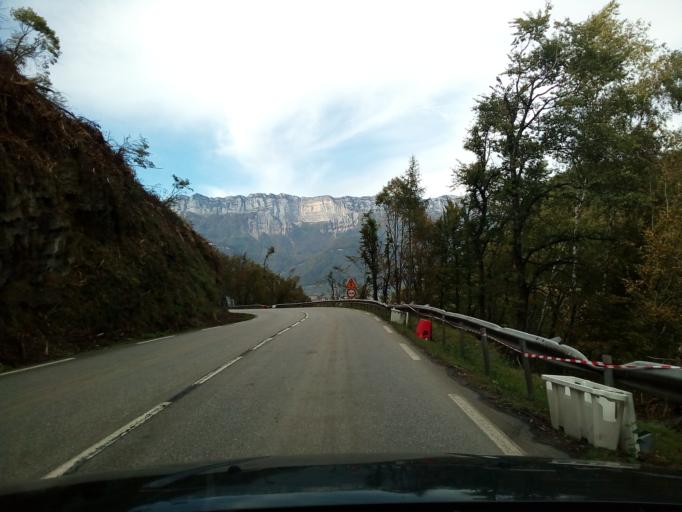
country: FR
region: Rhone-Alpes
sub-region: Departement de l'Isere
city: Le Cheylas
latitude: 45.3659
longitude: 6.0111
